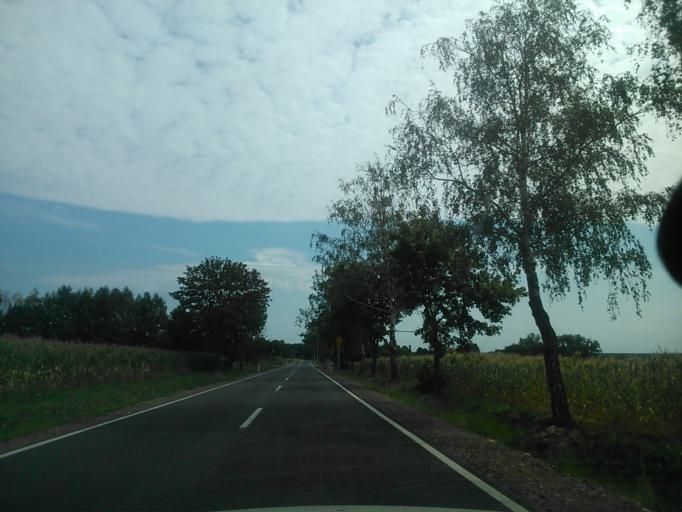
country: PL
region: Warmian-Masurian Voivodeship
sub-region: Powiat dzialdowski
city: Dzialdowo
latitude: 53.2343
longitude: 20.0208
